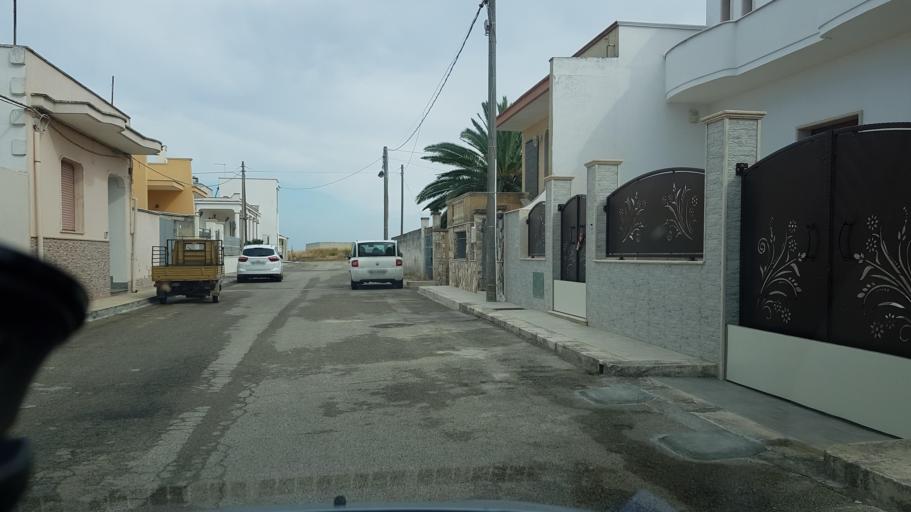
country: IT
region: Apulia
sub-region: Provincia di Brindisi
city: Torre Santa Susanna
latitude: 40.4741
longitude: 17.7414
